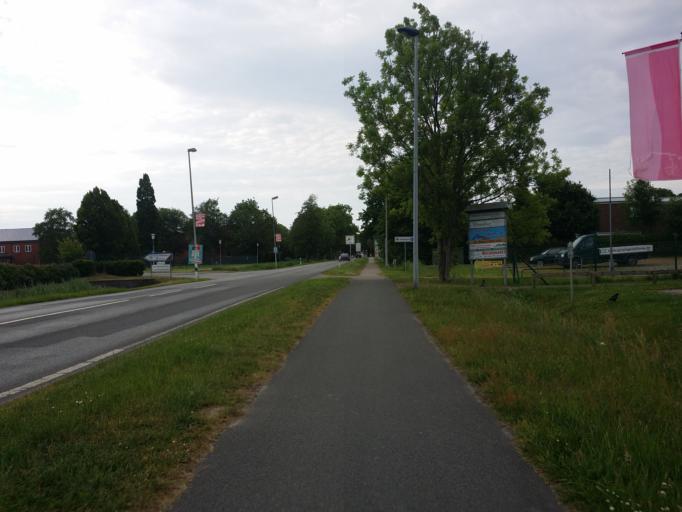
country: DE
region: Lower Saxony
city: Wittmund
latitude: 53.5692
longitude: 7.7834
